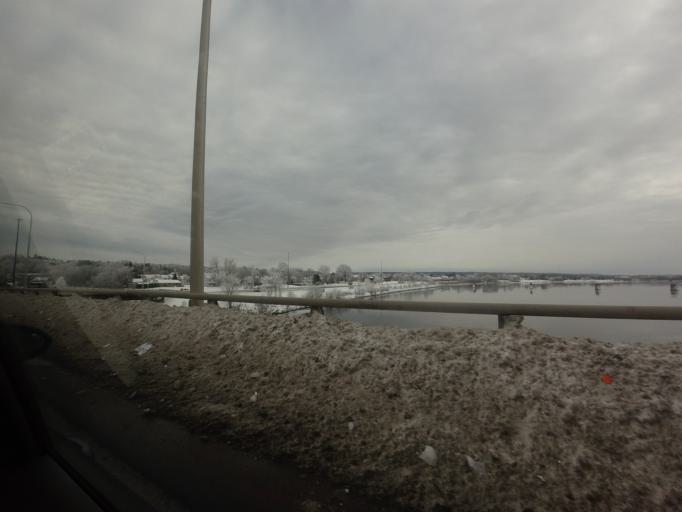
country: CA
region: New Brunswick
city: Fredericton
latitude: 45.9704
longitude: -66.6415
